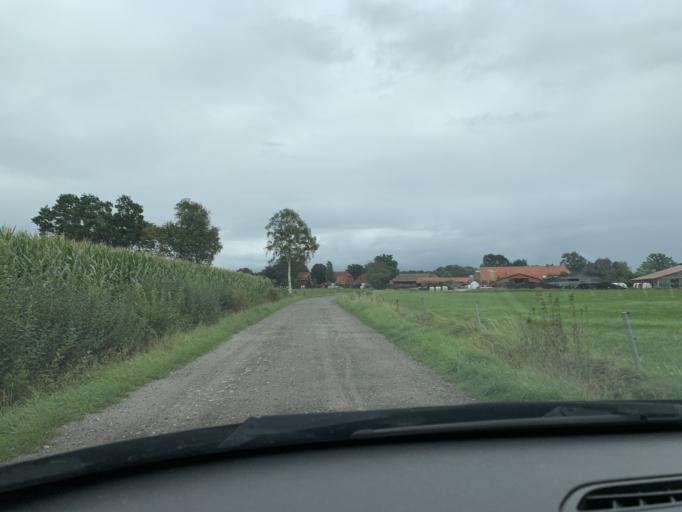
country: DE
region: Lower Saxony
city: Westerstede
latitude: 53.2454
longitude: 7.8837
